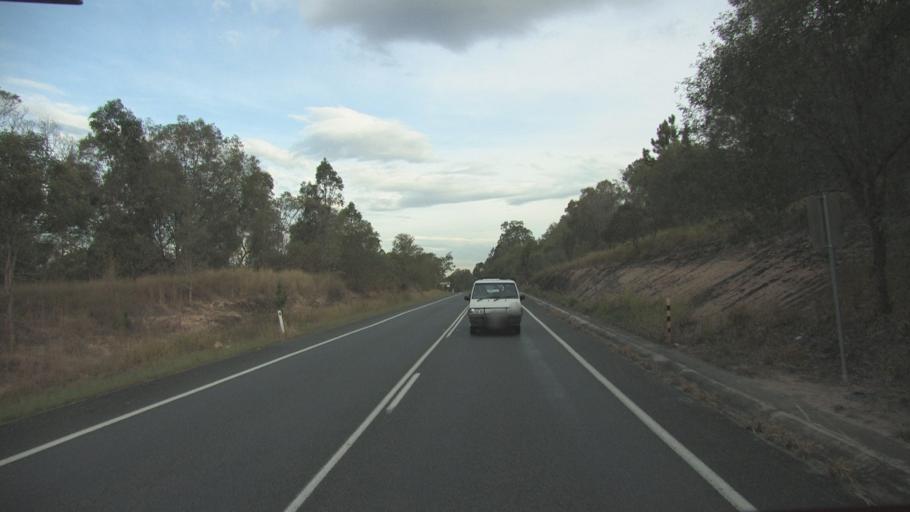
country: AU
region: Queensland
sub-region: Logan
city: Chambers Flat
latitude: -27.8337
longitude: 153.1070
